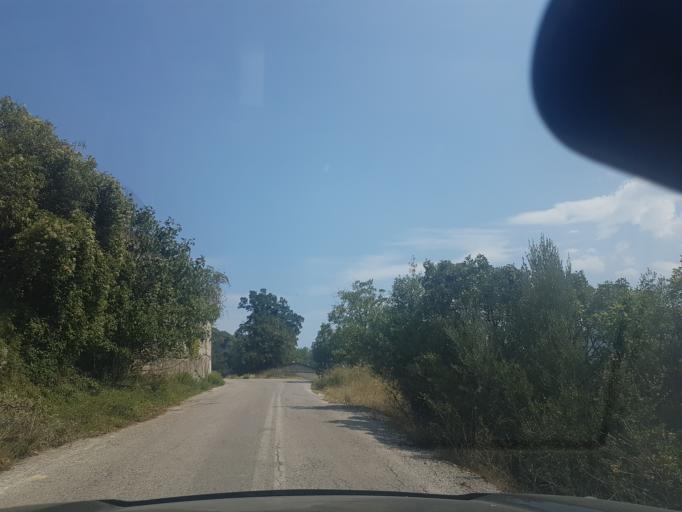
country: GR
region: Central Greece
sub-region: Nomos Evvoias
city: Yimnon
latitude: 38.6217
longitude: 23.8869
